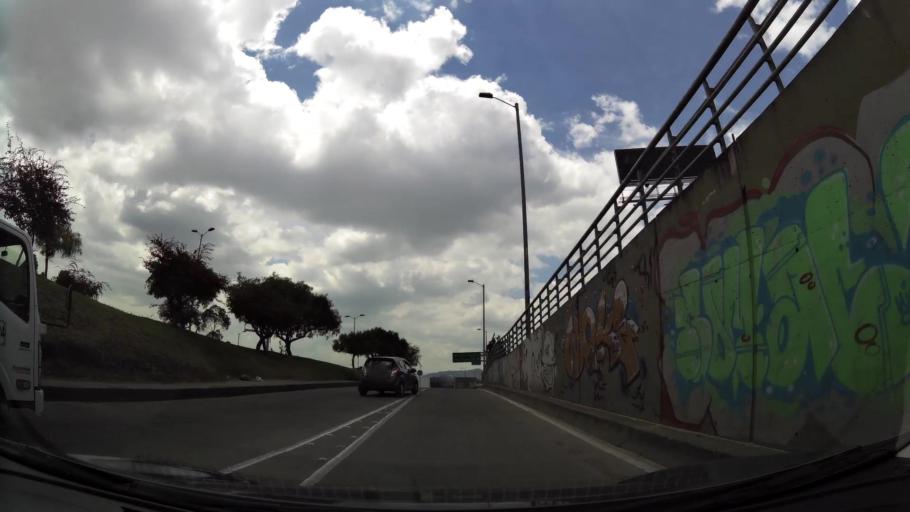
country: CO
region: Cundinamarca
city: Cota
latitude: 4.7364
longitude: -74.0816
